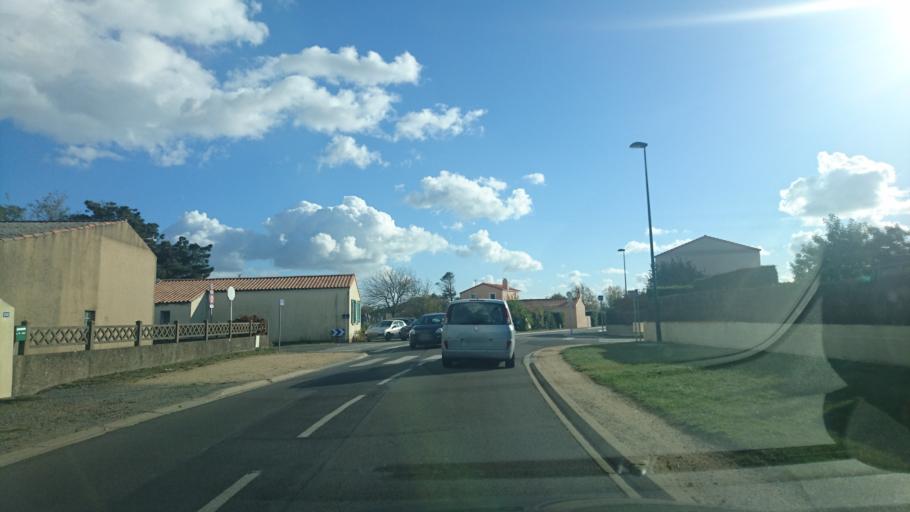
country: FR
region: Pays de la Loire
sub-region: Departement de la Vendee
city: Les Sables-d'Olonne
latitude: 46.5196
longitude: -1.7916
